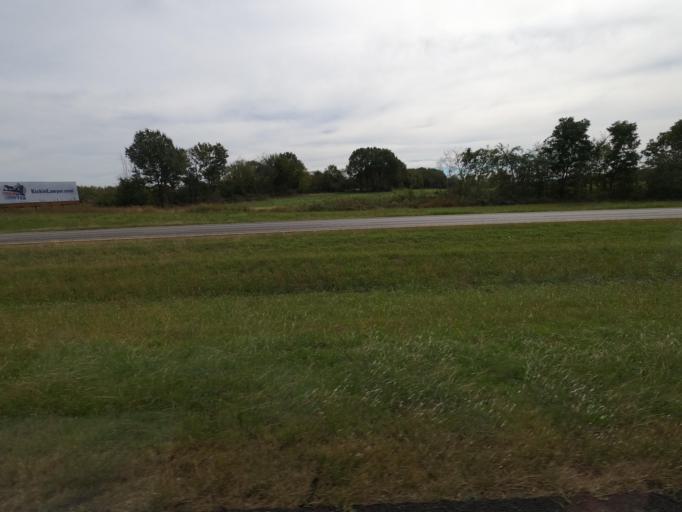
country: US
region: Tennessee
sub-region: Tipton County
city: Mason
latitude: 35.3790
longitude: -89.4459
